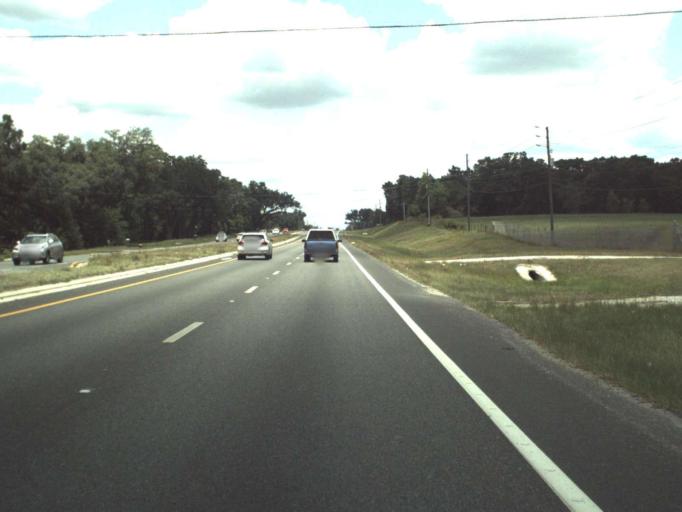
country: US
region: Florida
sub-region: Sumter County
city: Wildwood
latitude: 28.8916
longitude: -82.0369
